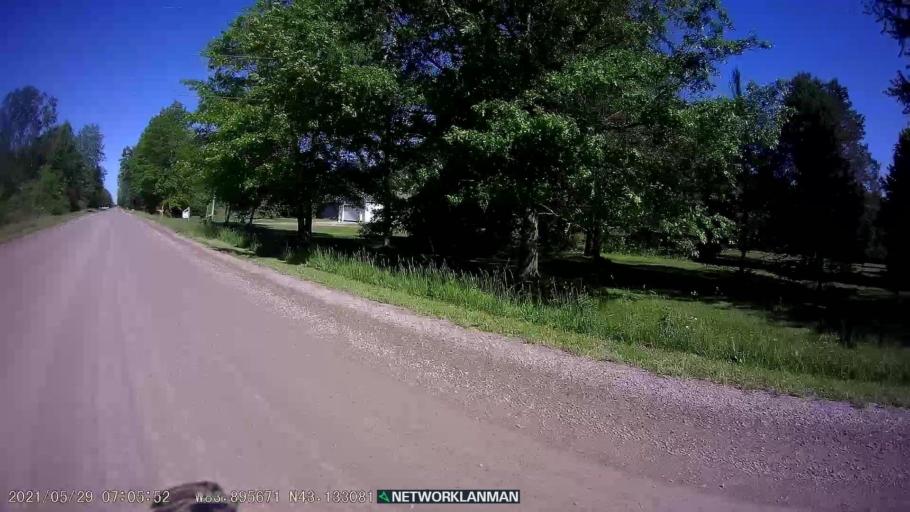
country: US
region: Michigan
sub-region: Genesee County
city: Montrose
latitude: 43.1331
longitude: -83.8961
